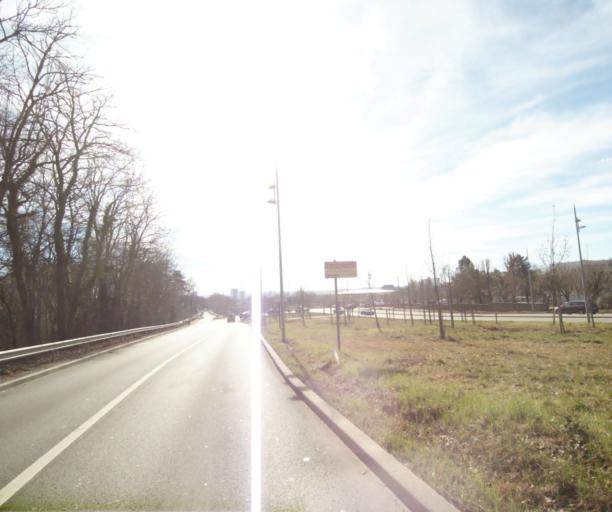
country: FR
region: Lorraine
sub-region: Departement de Meurthe-et-Moselle
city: Laxou
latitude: 48.7021
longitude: 6.1359
